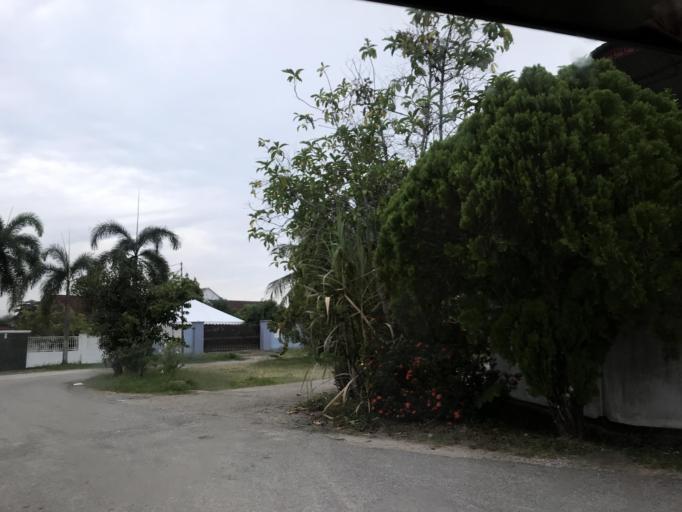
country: MY
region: Kelantan
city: Kota Bharu
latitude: 6.1162
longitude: 102.2093
